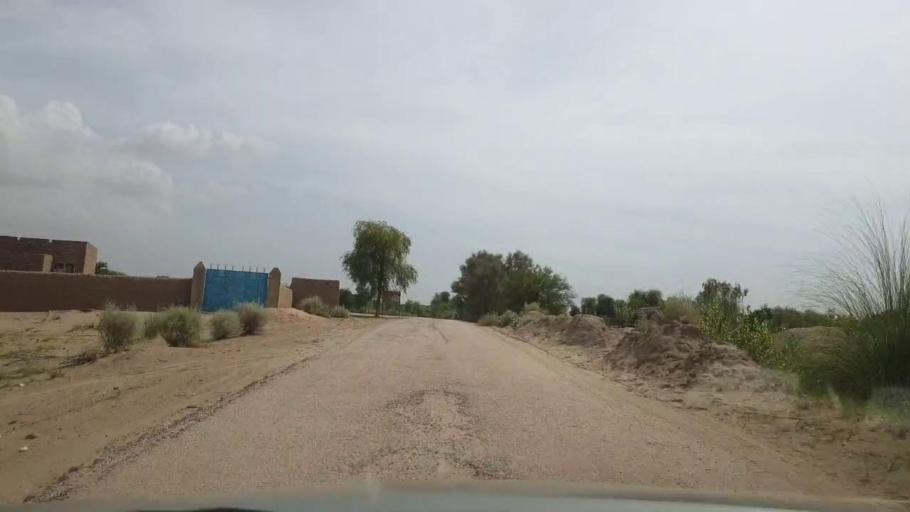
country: PK
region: Sindh
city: Kot Diji
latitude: 27.1198
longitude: 69.0256
